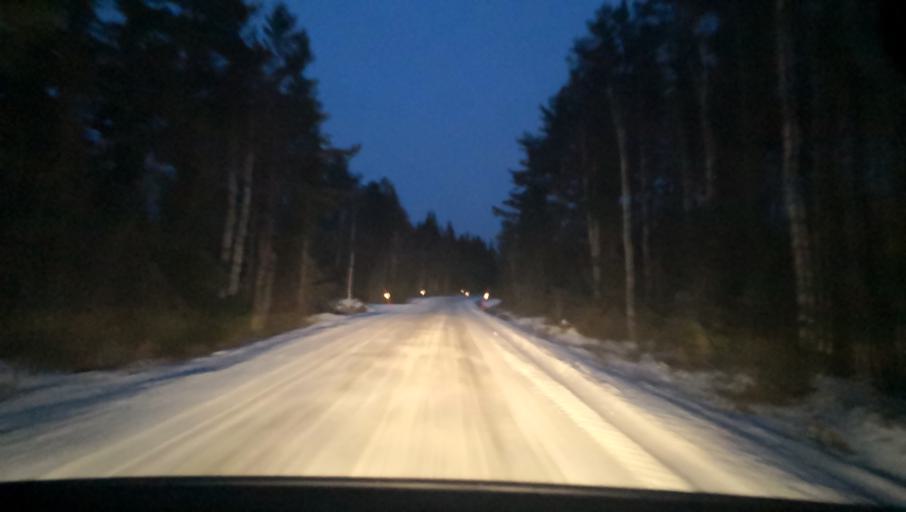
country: SE
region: Uppsala
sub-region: Heby Kommun
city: Tarnsjo
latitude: 60.2491
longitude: 16.7299
